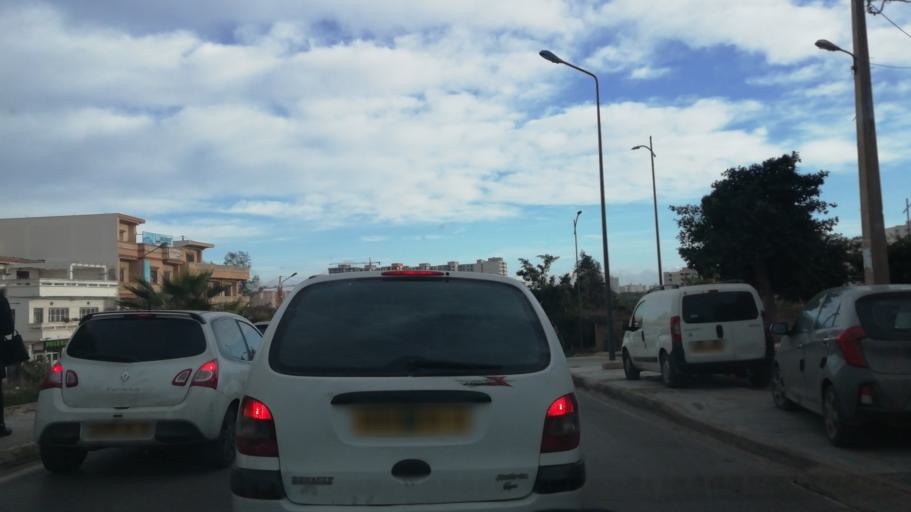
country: DZ
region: Oran
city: Bir el Djir
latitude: 35.7170
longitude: -0.5796
